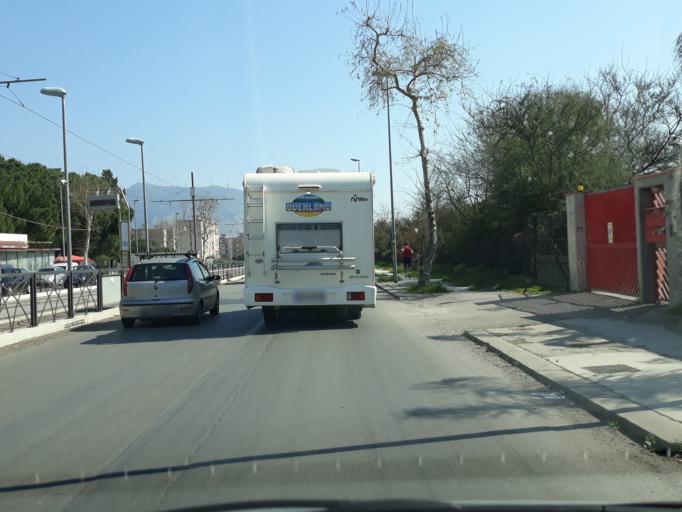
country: IT
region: Sicily
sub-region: Palermo
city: Palermo
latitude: 38.1313
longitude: 13.3053
